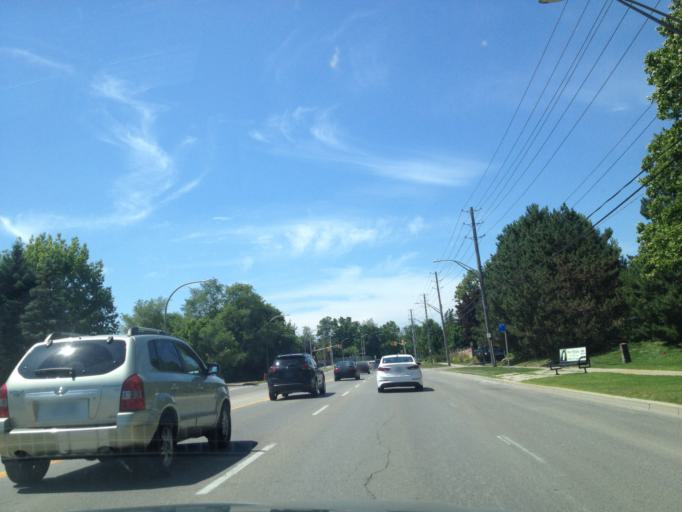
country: CA
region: Ontario
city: London
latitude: 43.0191
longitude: -81.2768
